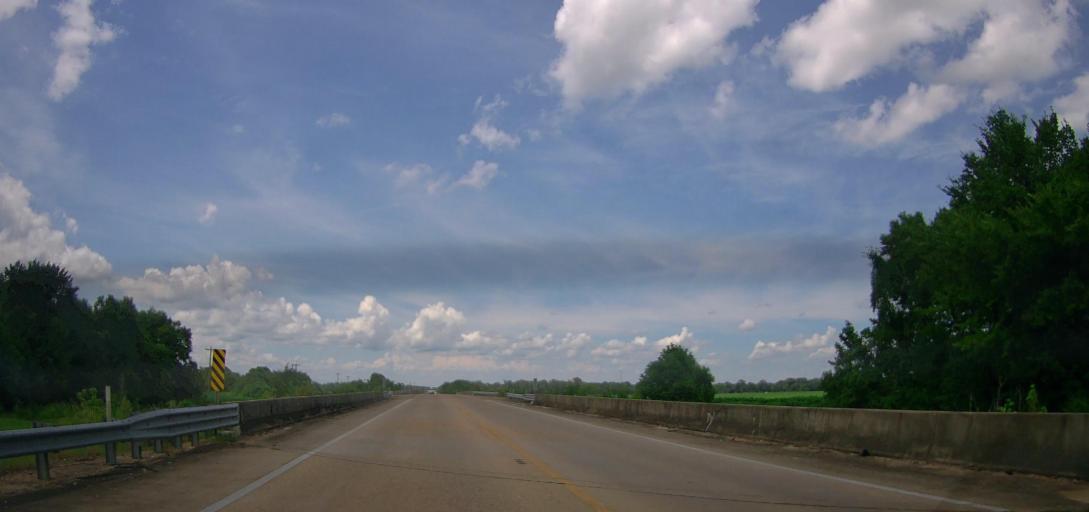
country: US
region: Mississippi
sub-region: Lee County
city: Shannon
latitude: 34.1368
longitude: -88.7194
